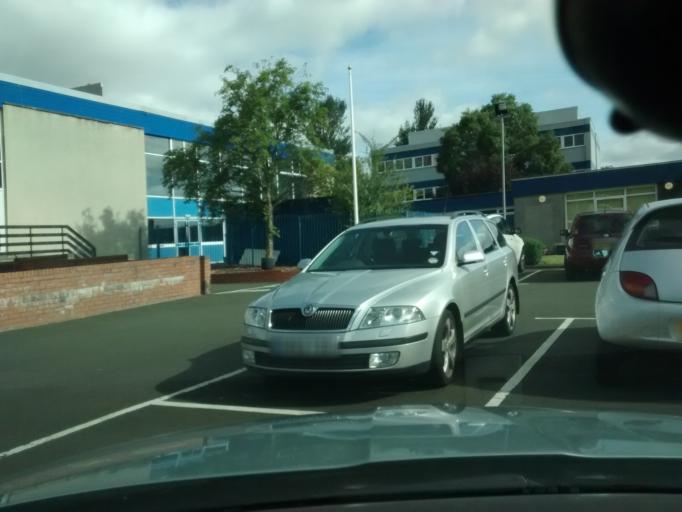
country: GB
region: Scotland
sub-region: West Lothian
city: Mid Calder
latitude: 55.8952
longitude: -3.5008
